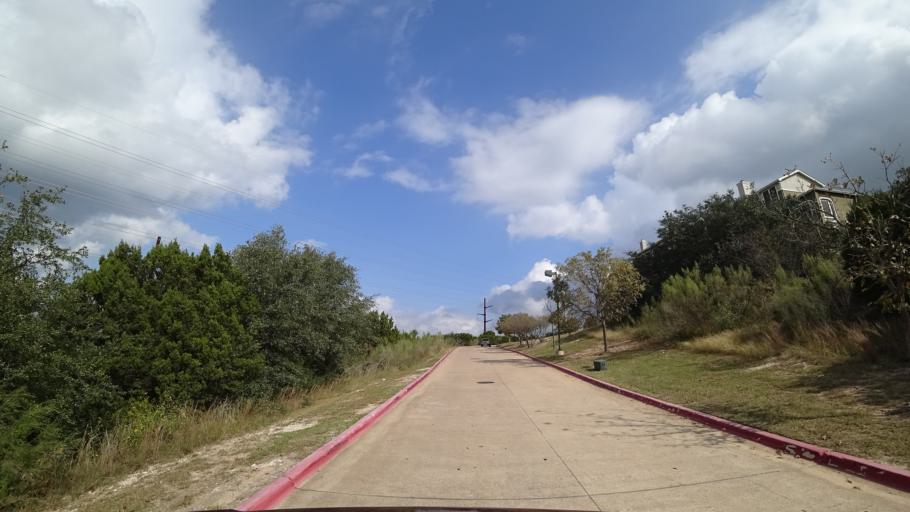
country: US
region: Texas
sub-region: Travis County
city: Hudson Bend
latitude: 30.3844
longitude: -97.8820
